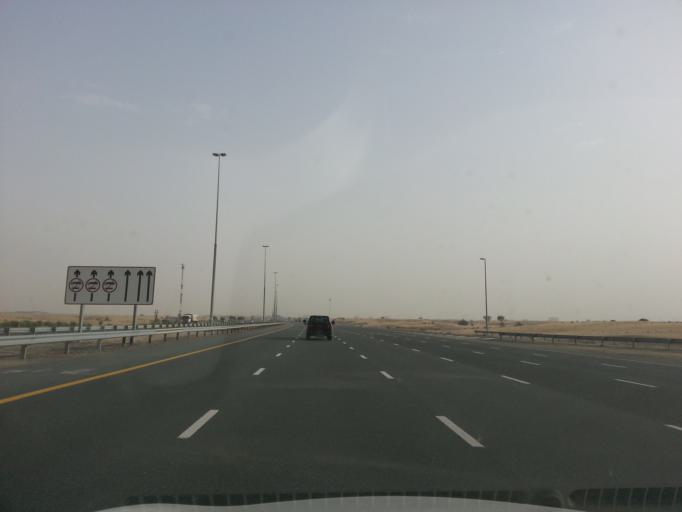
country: AE
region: Dubai
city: Dubai
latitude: 24.9775
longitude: 55.2397
